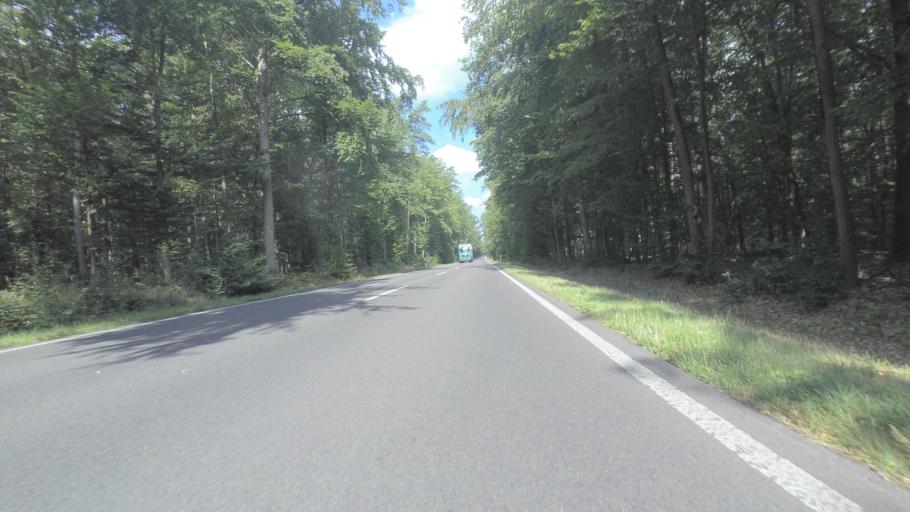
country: DE
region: Brandenburg
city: Walsleben
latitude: 52.9808
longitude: 12.7095
